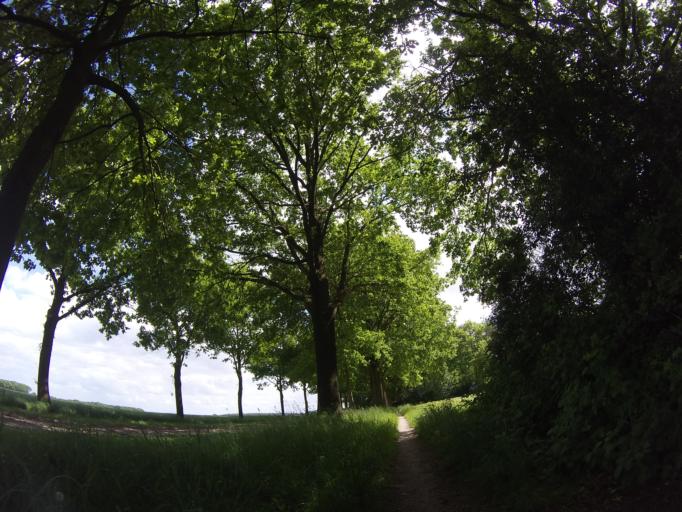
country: NL
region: Drenthe
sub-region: Gemeente Borger-Odoorn
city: Borger
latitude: 52.8800
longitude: 6.8702
